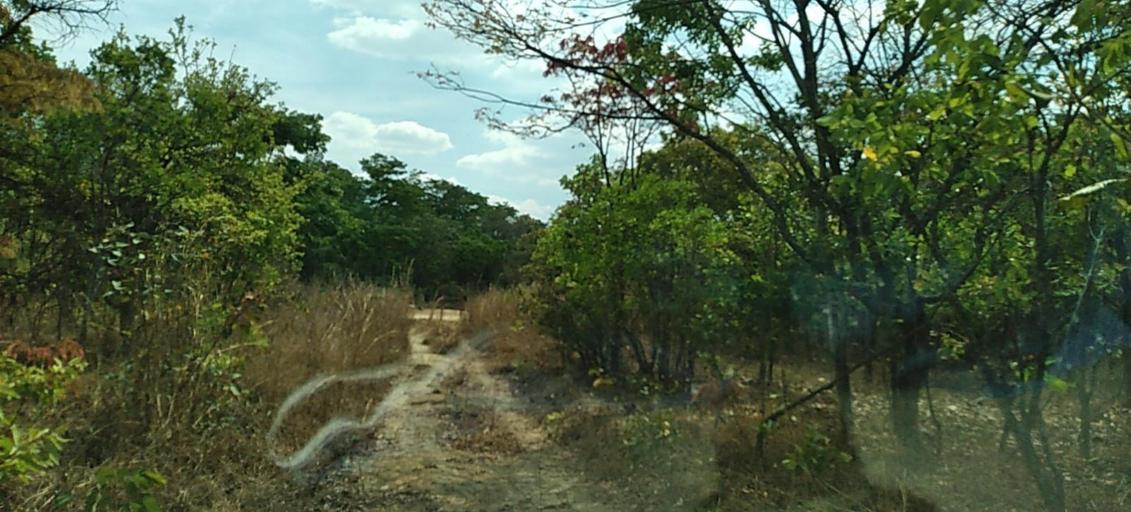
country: ZM
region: Copperbelt
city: Chililabombwe
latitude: -12.3325
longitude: 27.7620
